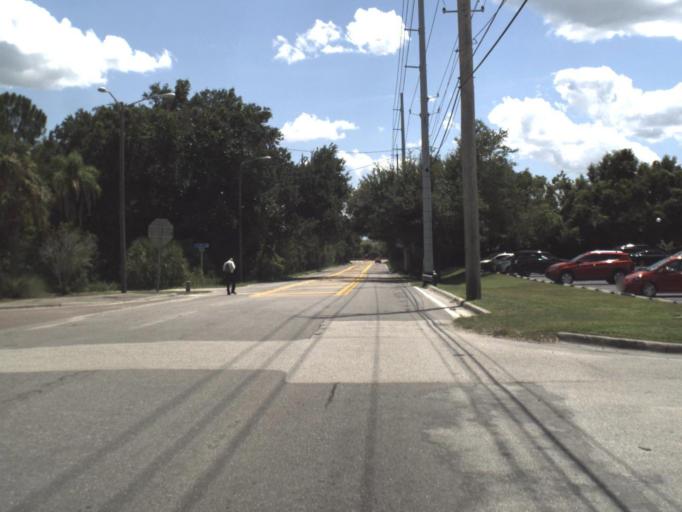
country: US
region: Florida
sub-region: Hillsborough County
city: Brandon
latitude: 27.9315
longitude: -82.3145
